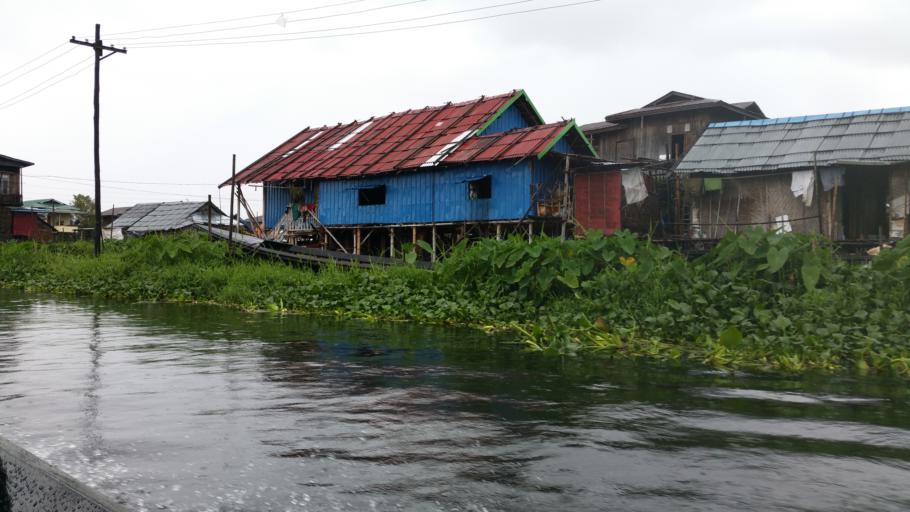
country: MM
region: Shan
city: Taunggyi
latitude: 20.5058
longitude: 96.9029
